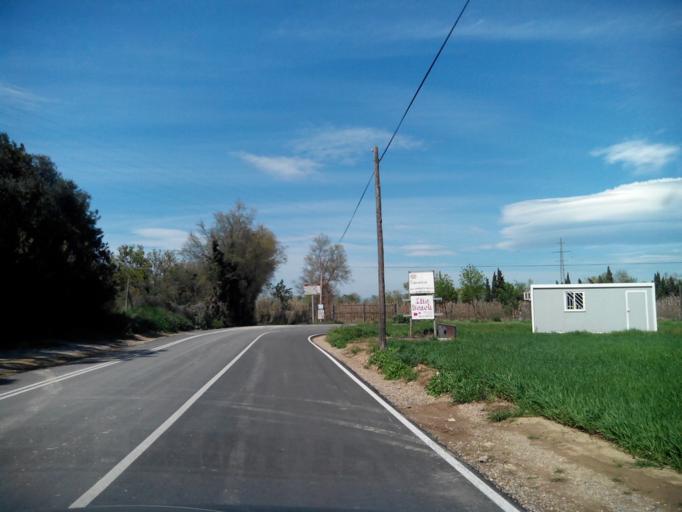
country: ES
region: Catalonia
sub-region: Provincia de Girona
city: Sant Pere Pescador
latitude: 42.1868
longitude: 3.0915
